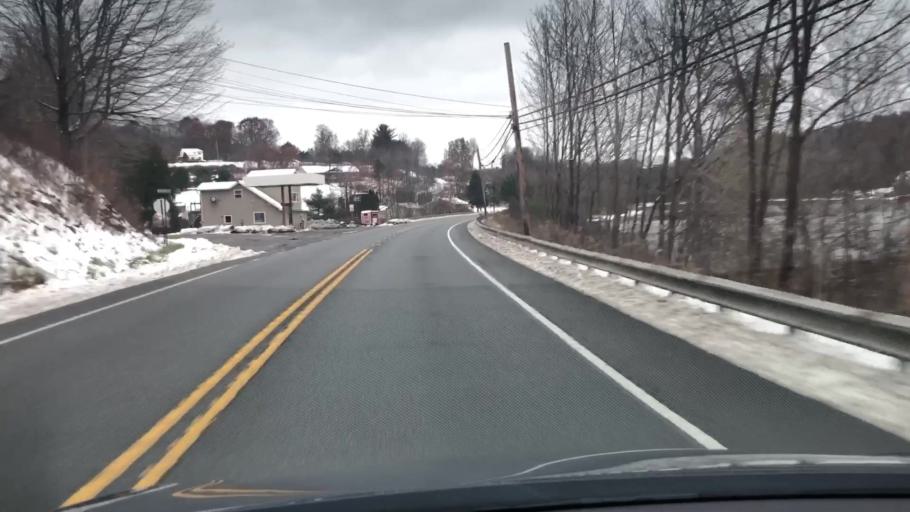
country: US
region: Pennsylvania
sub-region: Clearfield County
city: Treasure Lake
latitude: 41.1581
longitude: -78.6679
